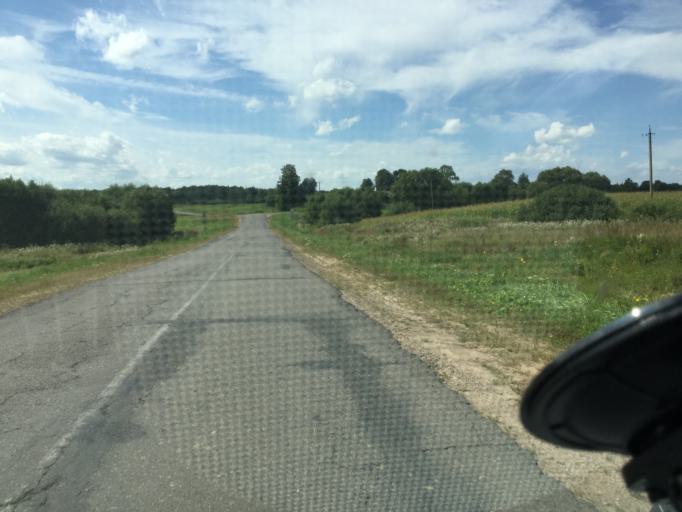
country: BY
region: Vitebsk
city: Chashniki
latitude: 55.3111
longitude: 29.4121
